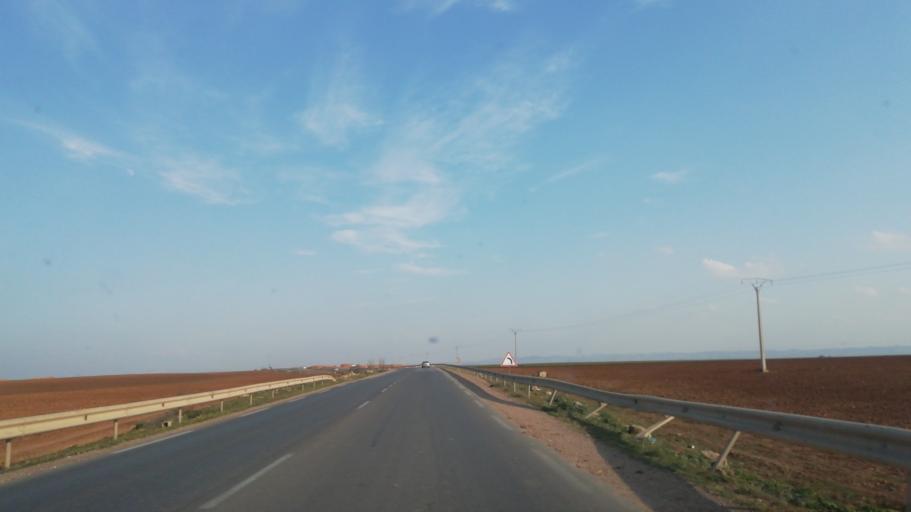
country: DZ
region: Relizane
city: Relizane
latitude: 35.8920
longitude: 0.6190
